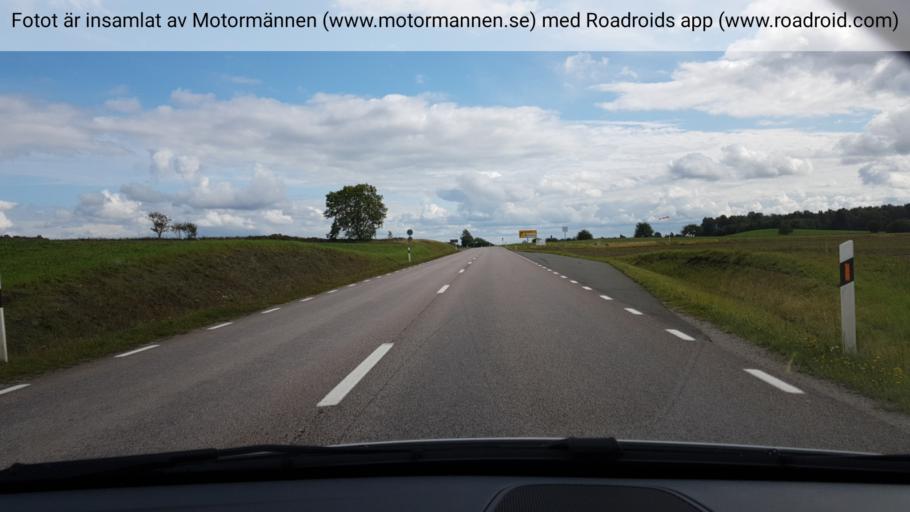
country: SE
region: Vaestra Goetaland
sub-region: Falkopings Kommun
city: Falkoeping
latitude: 58.1508
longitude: 13.6038
